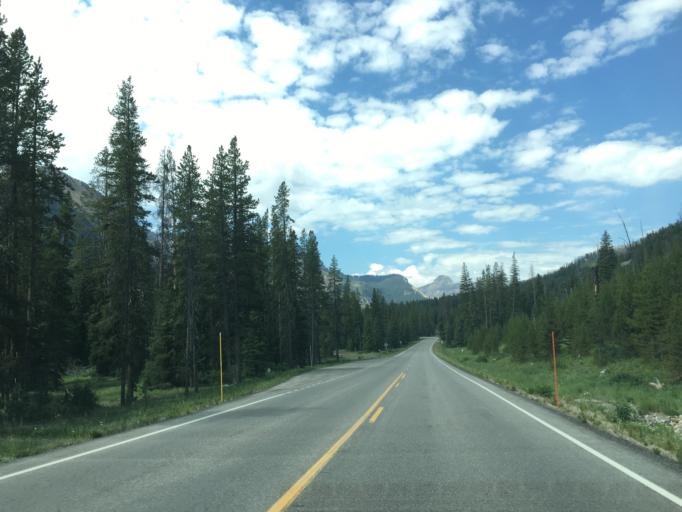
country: US
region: Montana
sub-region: Stillwater County
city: Absarokee
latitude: 45.0180
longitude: -109.9628
